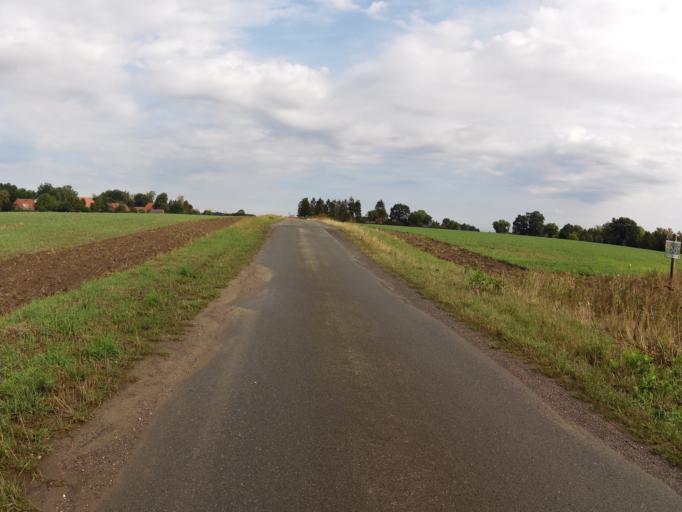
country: DE
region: Lower Saxony
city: Marklohe
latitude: 52.6686
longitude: 9.1673
